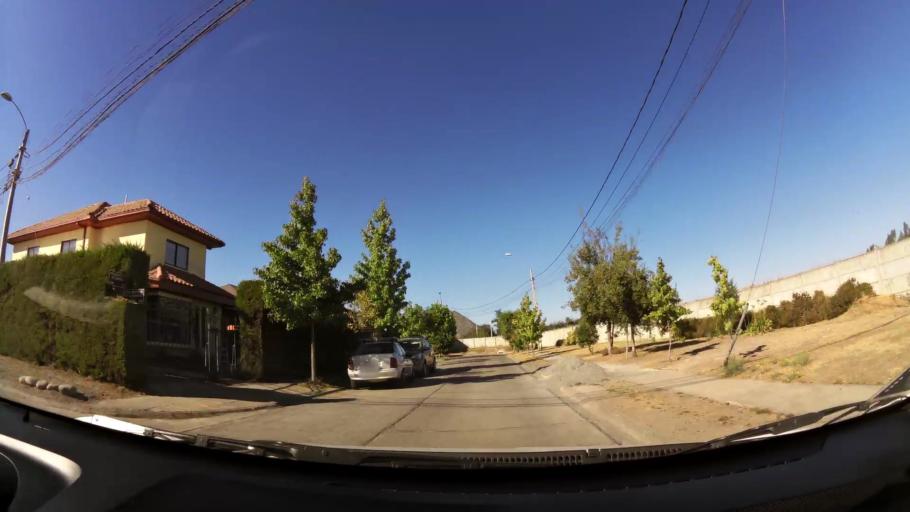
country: CL
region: O'Higgins
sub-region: Provincia de Cachapoal
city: Rancagua
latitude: -34.1948
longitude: -70.7205
